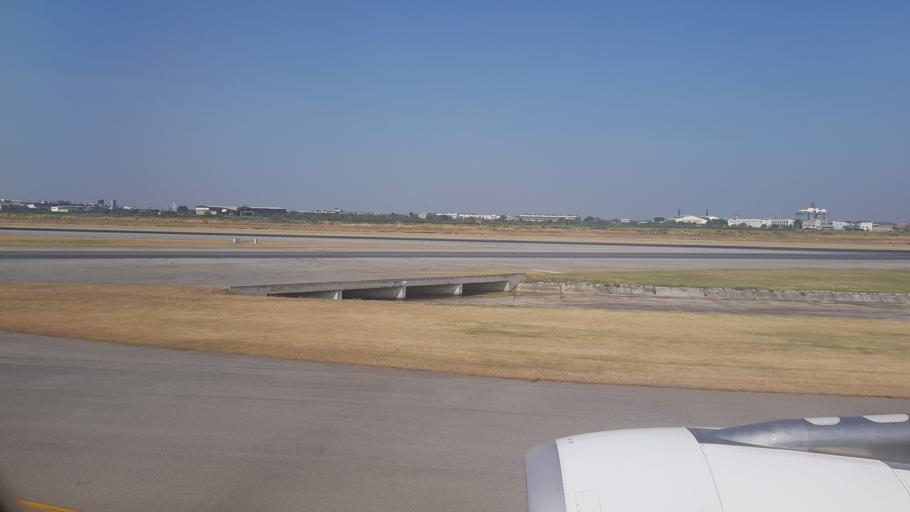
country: TH
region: Bangkok
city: Lat Krabang
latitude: 13.6829
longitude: 100.7396
